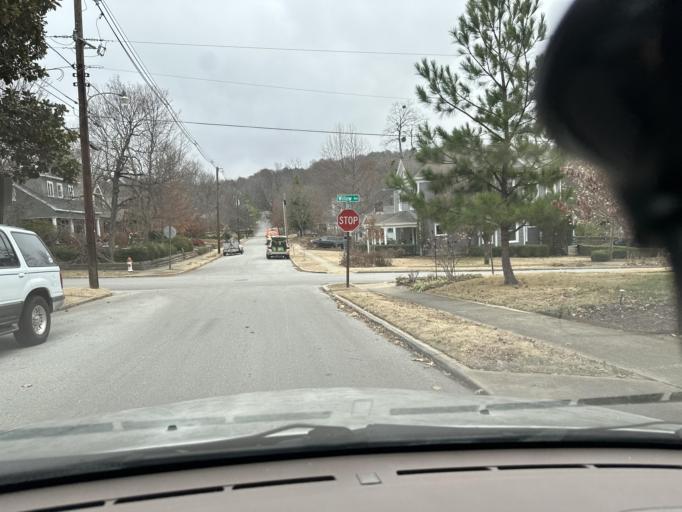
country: US
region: Arkansas
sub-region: Washington County
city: Fayetteville
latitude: 36.0674
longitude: -94.1549
